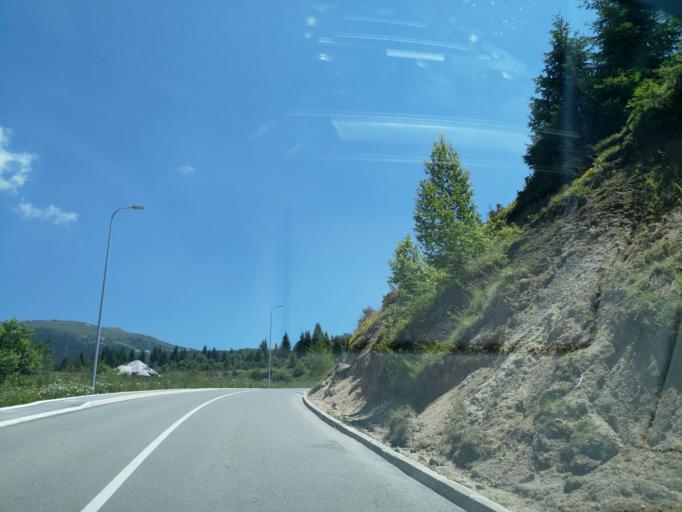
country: RS
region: Central Serbia
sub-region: Raski Okrug
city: Raska
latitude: 43.2732
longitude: 20.7716
